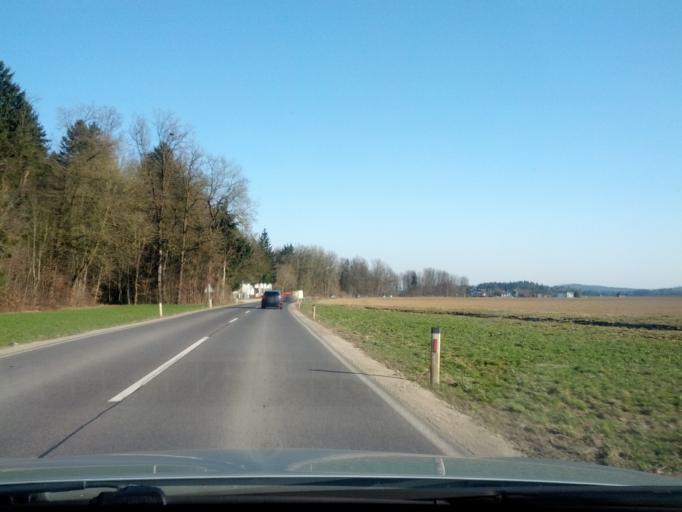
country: SI
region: Cerklje na Gorenjskem
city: Cerklje na Gorenjskem
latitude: 46.2244
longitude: 14.4933
